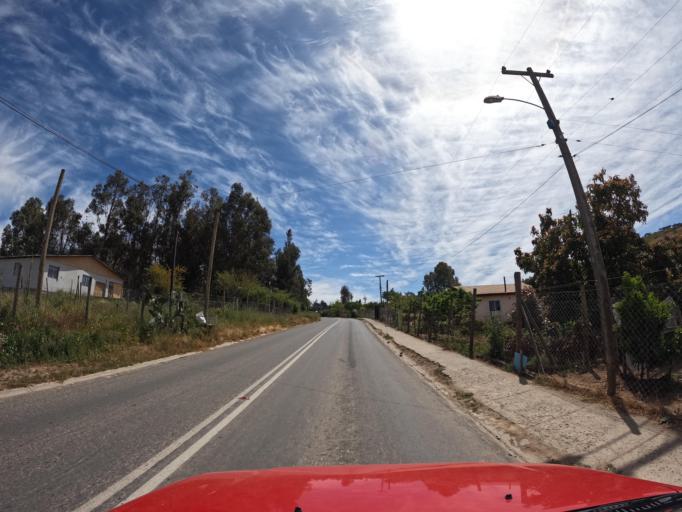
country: CL
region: Maule
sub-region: Provincia de Talca
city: Talca
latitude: -35.1192
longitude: -71.6852
